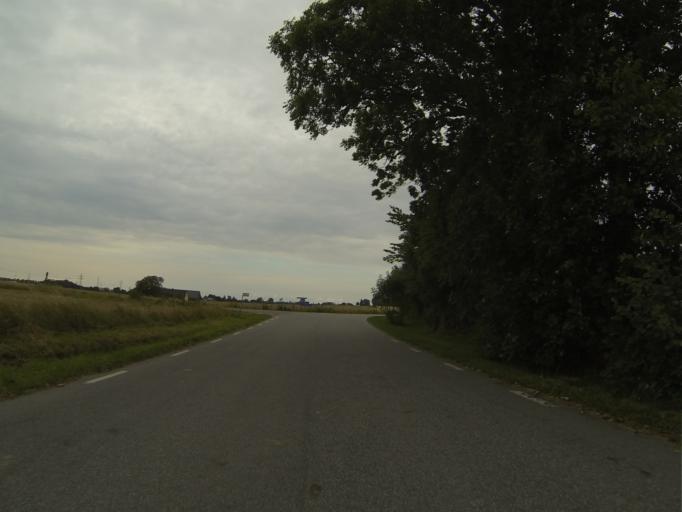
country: SE
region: Skane
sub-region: Staffanstorps Kommun
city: Hjaerup
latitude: 55.6566
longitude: 13.1604
